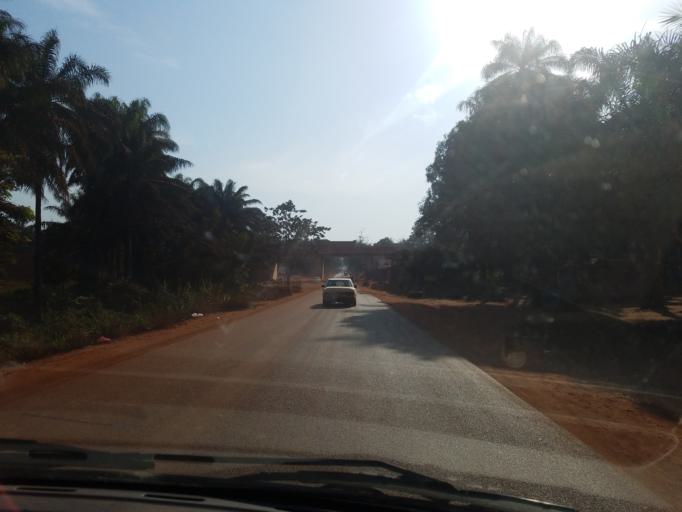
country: GN
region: Boke
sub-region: Boke Prefecture
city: Sangueya
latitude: 10.8126
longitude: -14.3836
